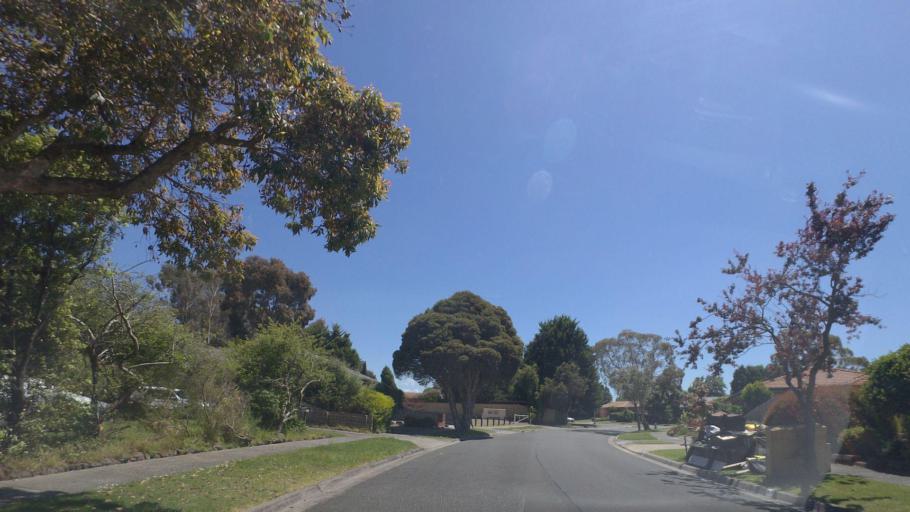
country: AU
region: Victoria
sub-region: Knox
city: Knoxfield
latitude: -37.8988
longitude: 145.2603
